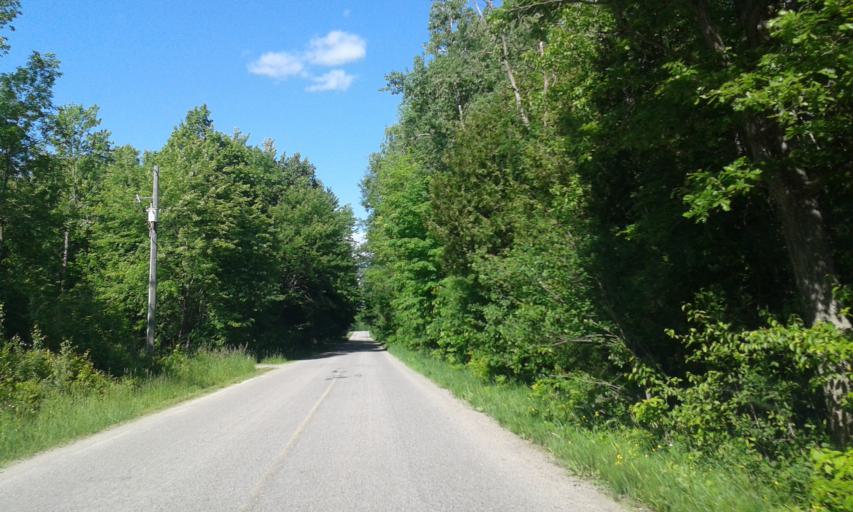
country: CA
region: Ontario
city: Brockville
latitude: 44.6262
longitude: -75.7408
